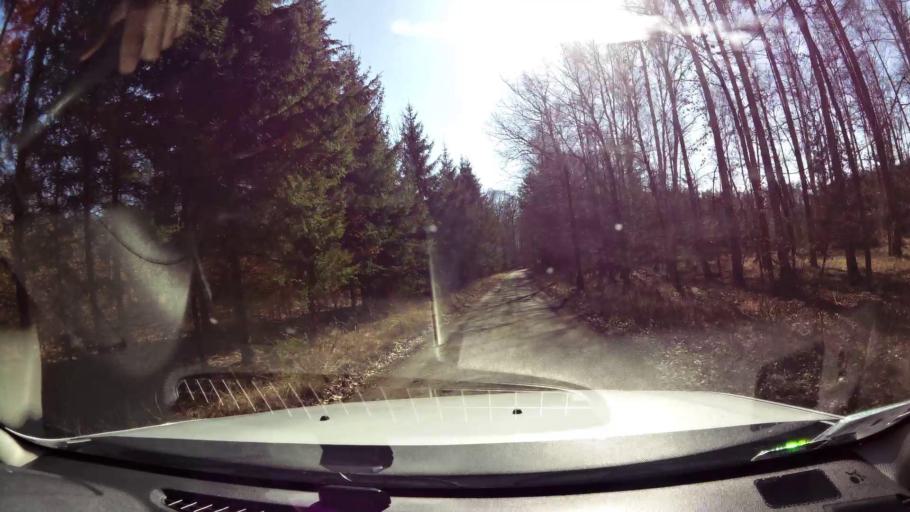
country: PL
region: West Pomeranian Voivodeship
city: Trzcinsko Zdroj
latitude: 53.0285
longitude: 14.6350
